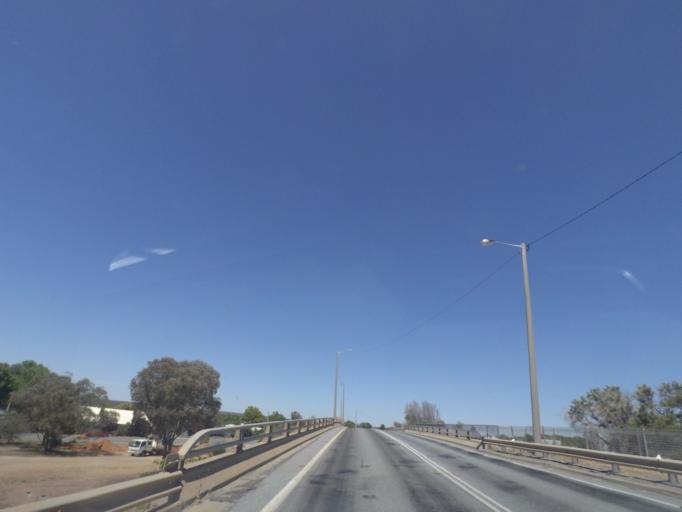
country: AU
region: New South Wales
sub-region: Narrandera
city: Narrandera
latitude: -34.7403
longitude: 146.5598
